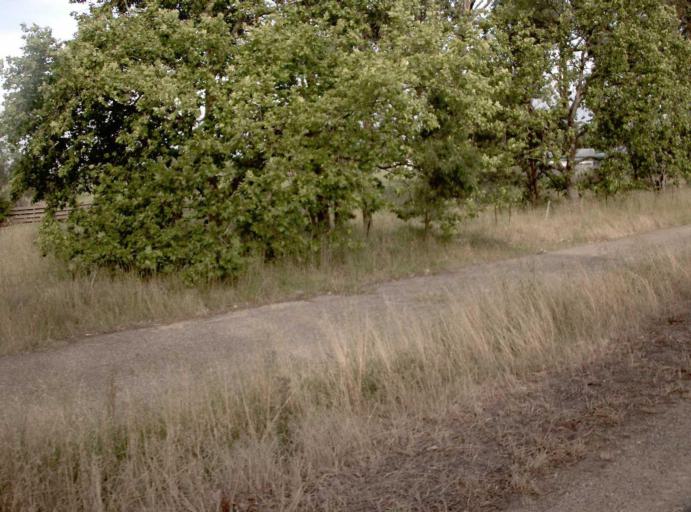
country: AU
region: Victoria
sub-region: Wellington
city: Heyfield
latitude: -37.9638
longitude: 146.8992
